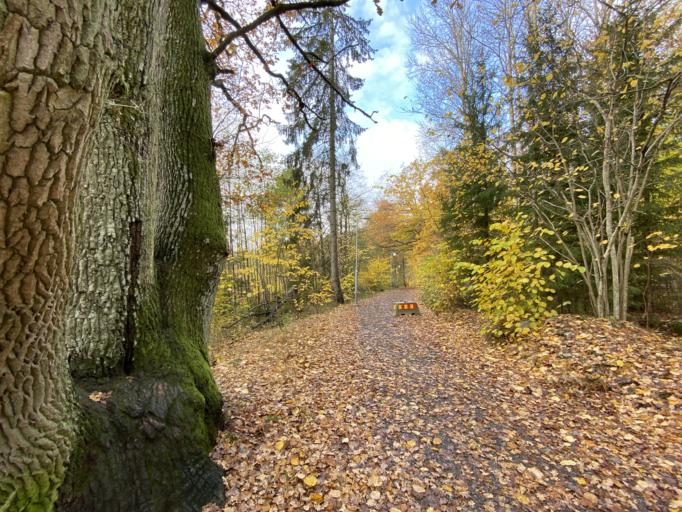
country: SE
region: Stockholm
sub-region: Salems Kommun
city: Ronninge
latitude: 59.1875
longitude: 17.7296
